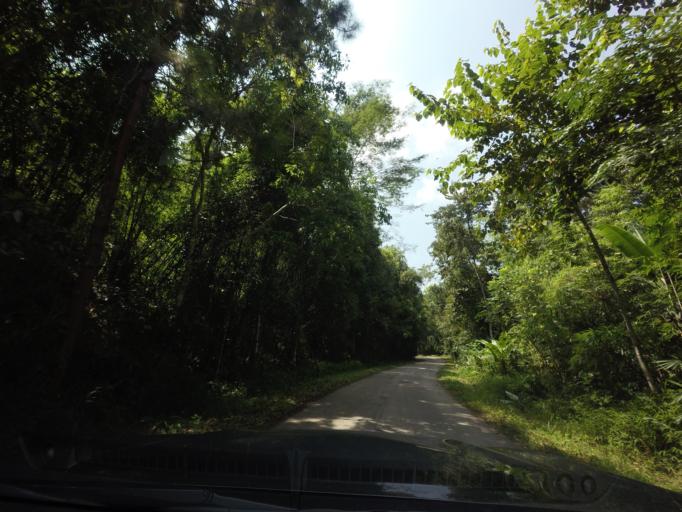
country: TH
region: Loei
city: Na Haeo
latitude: 17.4810
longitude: 100.9396
